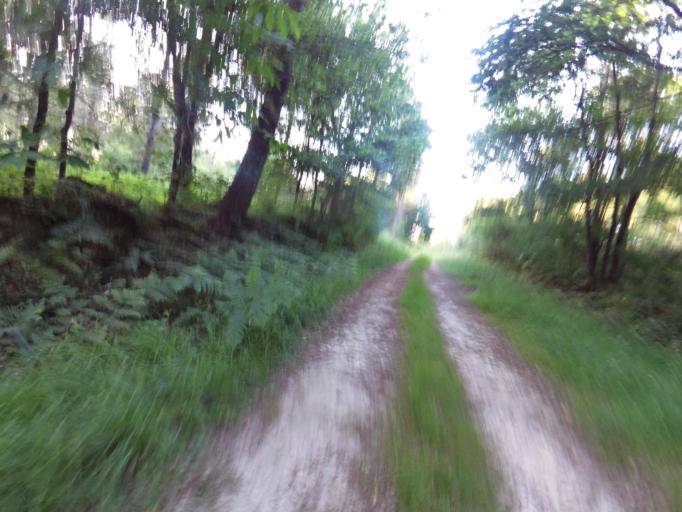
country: FR
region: Brittany
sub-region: Departement du Morbihan
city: Molac
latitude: 47.7539
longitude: -2.4119
